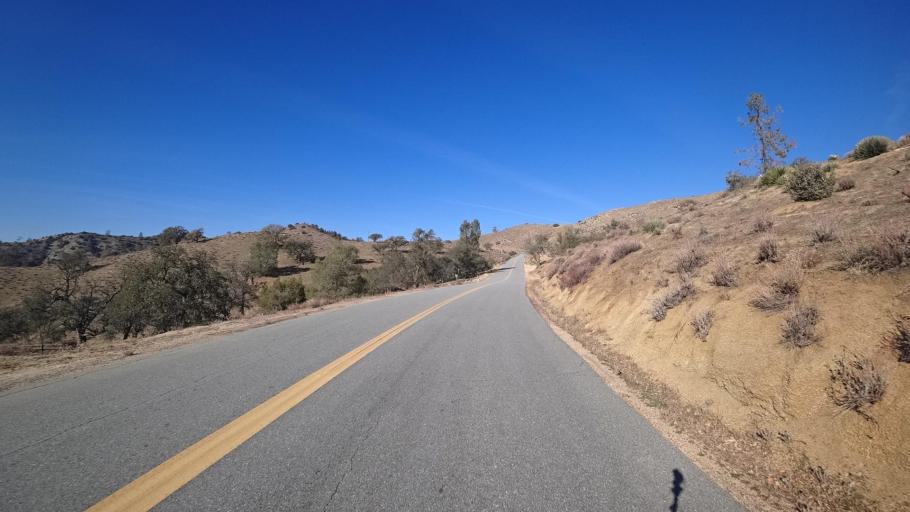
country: US
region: California
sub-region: Kern County
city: Bodfish
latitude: 35.3808
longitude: -118.4060
